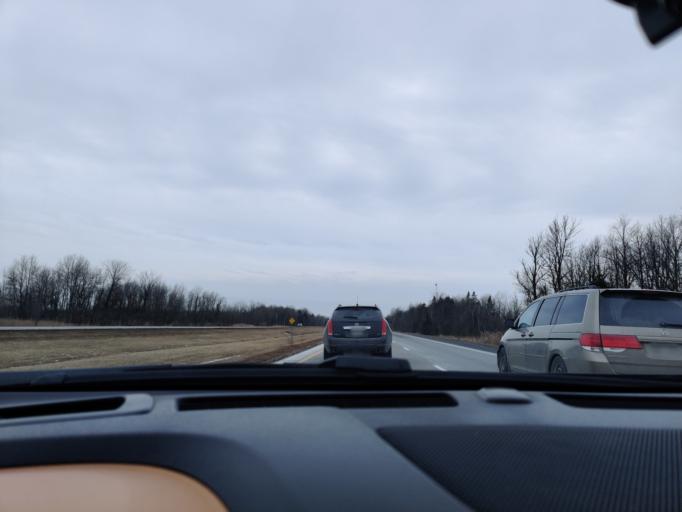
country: US
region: New York
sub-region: St. Lawrence County
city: Massena
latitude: 44.9922
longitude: -75.0457
